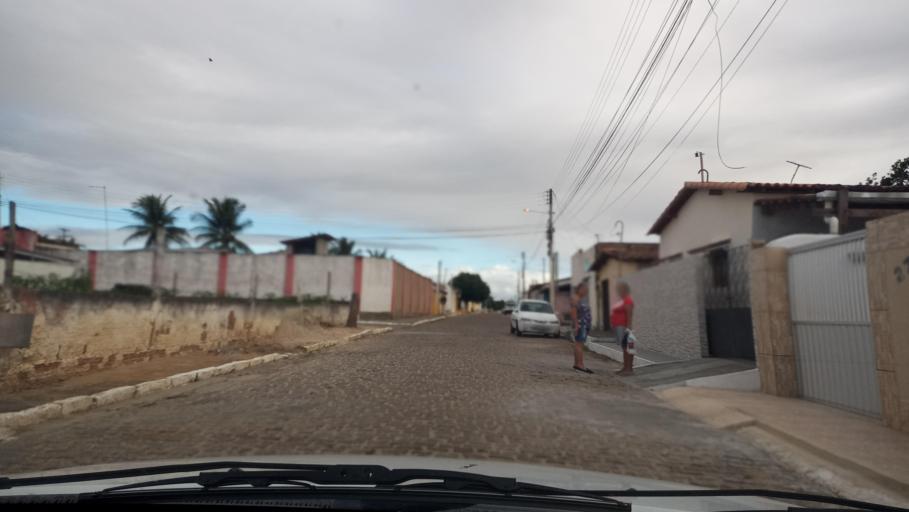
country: BR
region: Rio Grande do Norte
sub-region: Brejinho
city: Brejinho
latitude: -6.0461
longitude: -35.4329
